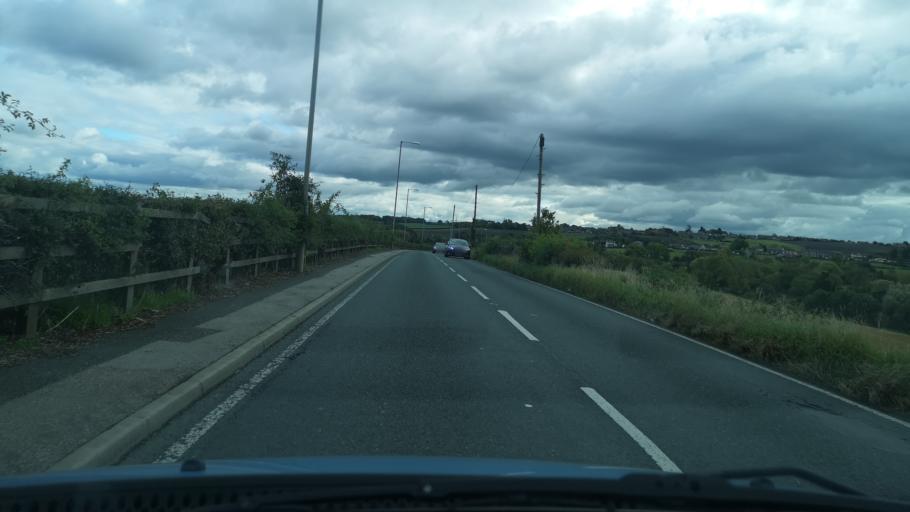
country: GB
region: England
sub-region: City and Borough of Wakefield
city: Middlestown
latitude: 53.6597
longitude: -1.5894
